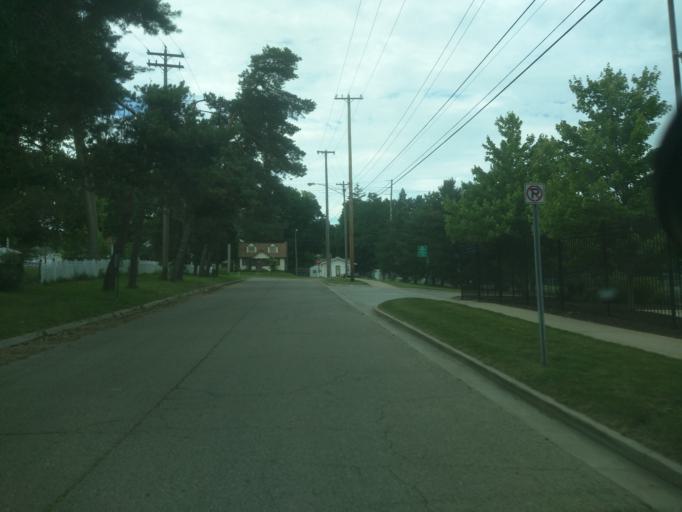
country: US
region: Michigan
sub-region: Ingham County
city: Lansing
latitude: 42.6894
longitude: -84.5346
